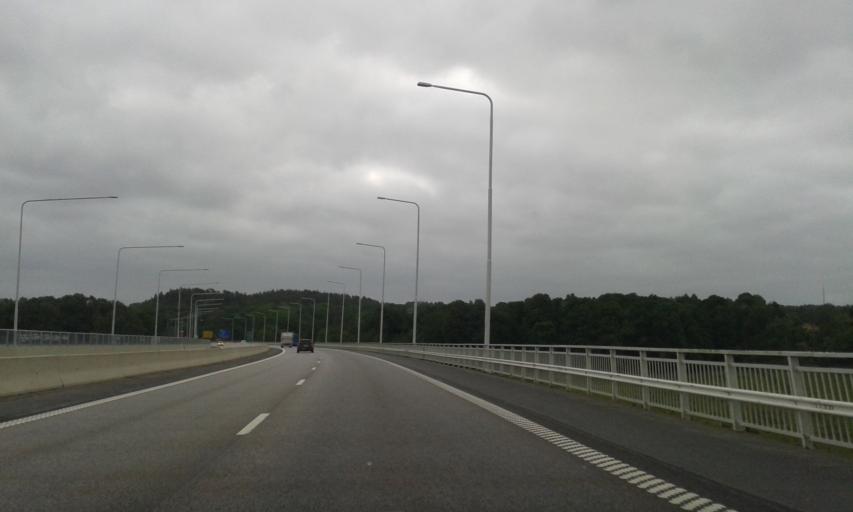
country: SE
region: Vaestra Goetaland
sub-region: Kungalvs Kommun
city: Kungalv
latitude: 57.8645
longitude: 11.9733
